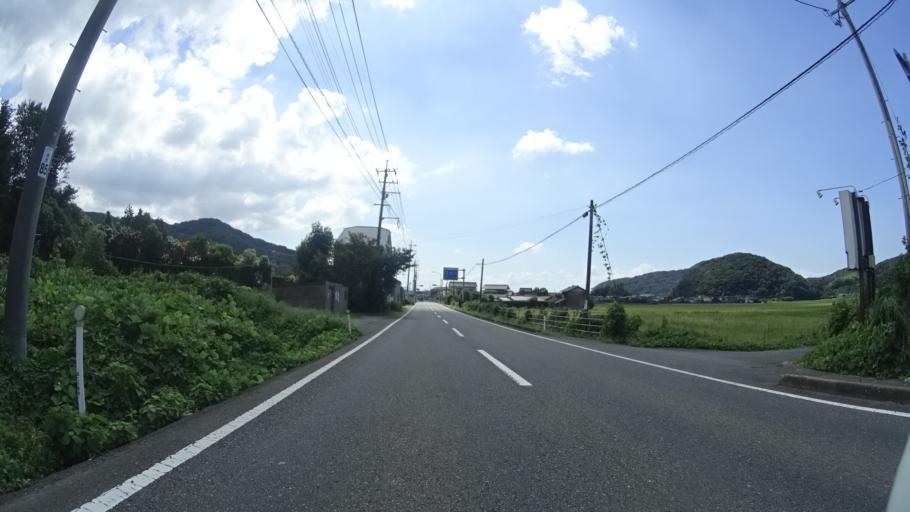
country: JP
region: Yamaguchi
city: Shimonoseki
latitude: 34.0797
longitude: 130.8953
